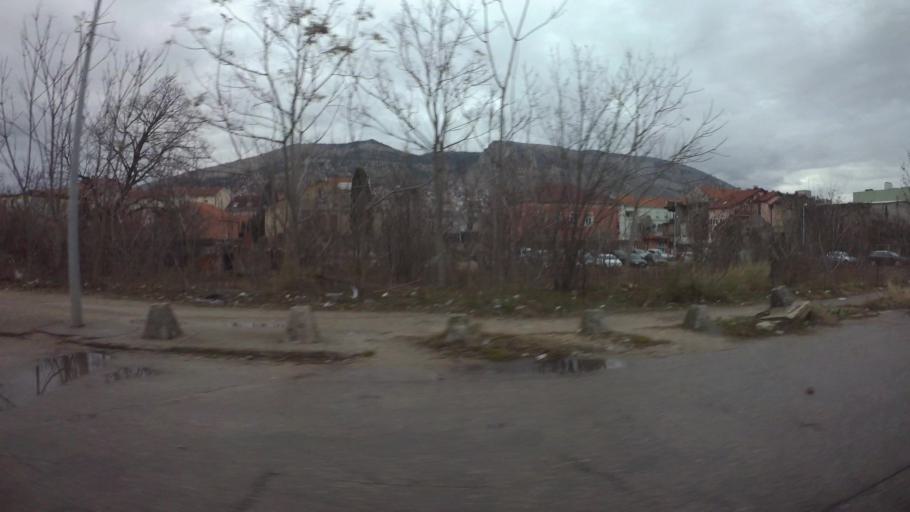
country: BA
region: Federation of Bosnia and Herzegovina
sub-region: Hercegovacko-Bosanski Kanton
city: Mostar
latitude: 43.3451
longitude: 17.8077
